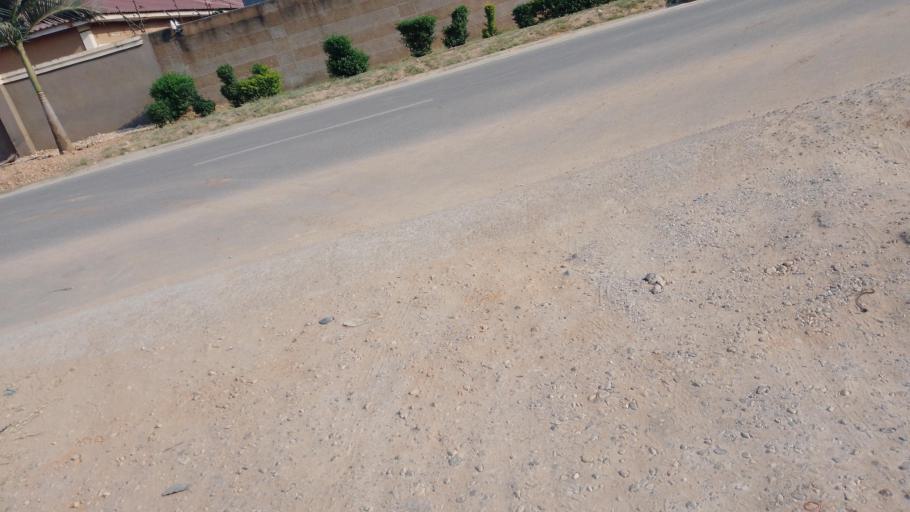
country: ZM
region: Lusaka
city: Lusaka
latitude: -15.3976
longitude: 28.3863
